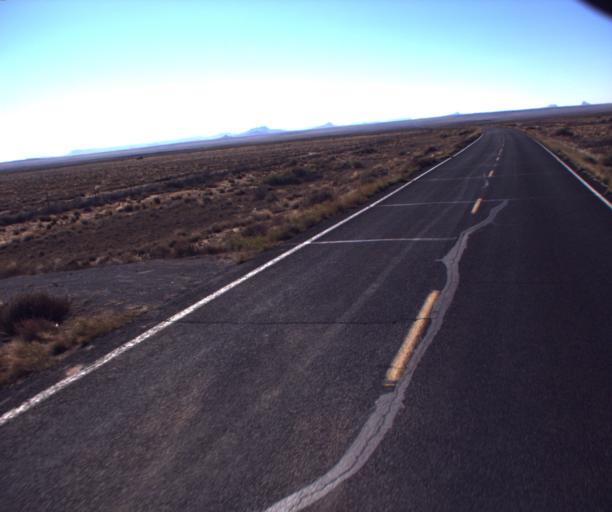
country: US
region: Arizona
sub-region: Navajo County
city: First Mesa
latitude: 35.7326
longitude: -110.5188
